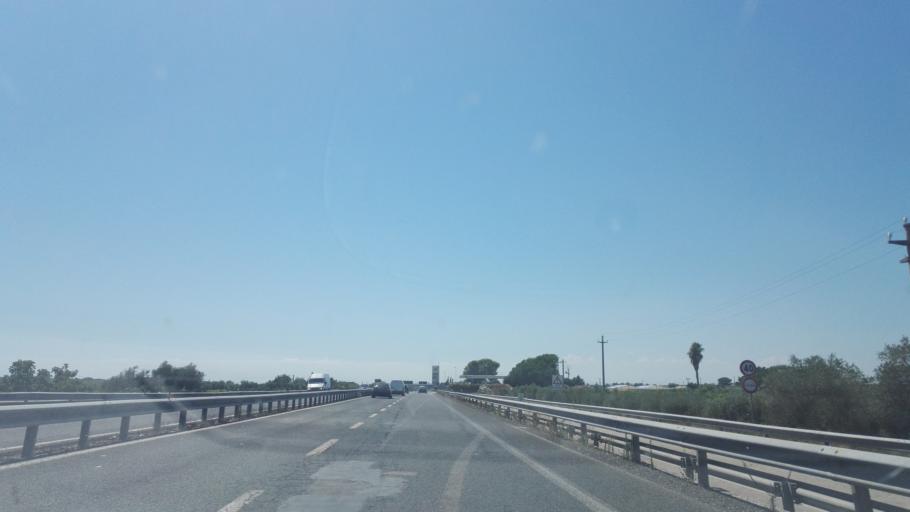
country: IT
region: Apulia
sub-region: Provincia di Taranto
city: Palagiano
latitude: 40.5243
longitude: 17.0357
